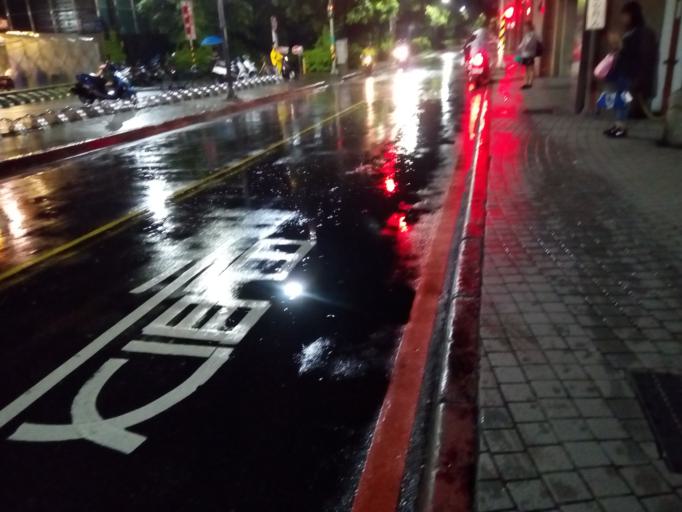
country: TW
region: Taiwan
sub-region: Keelung
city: Keelung
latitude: 25.0678
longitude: 121.6616
